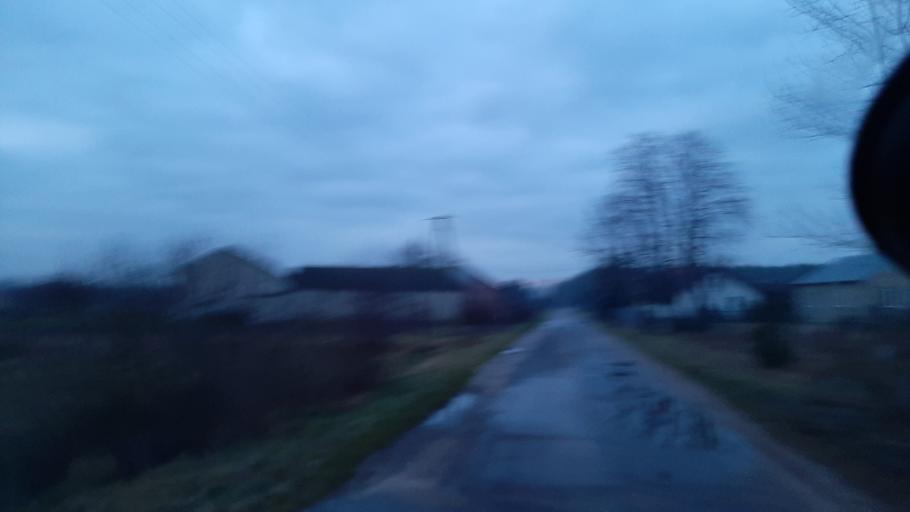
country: PL
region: Lublin Voivodeship
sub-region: Powiat lubartowski
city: Firlej
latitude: 51.5951
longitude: 22.5232
